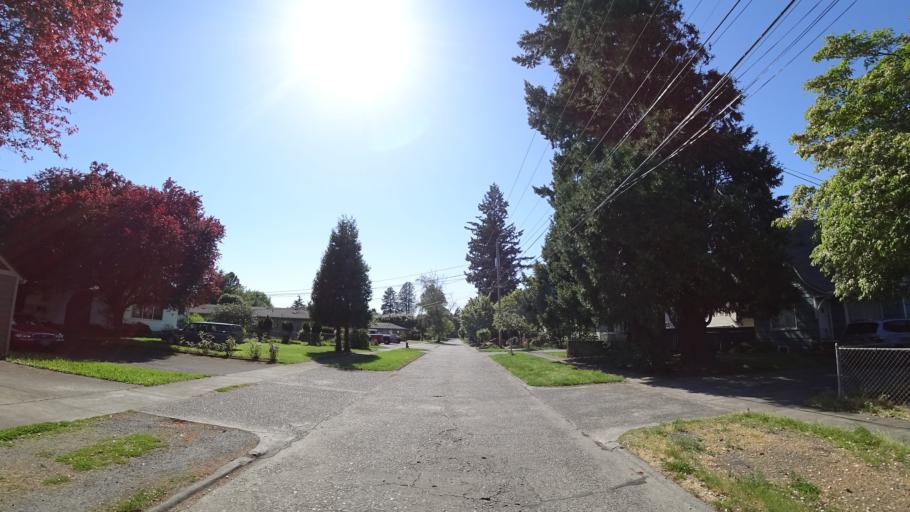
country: US
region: Oregon
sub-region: Multnomah County
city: Lents
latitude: 45.4879
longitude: -122.6060
